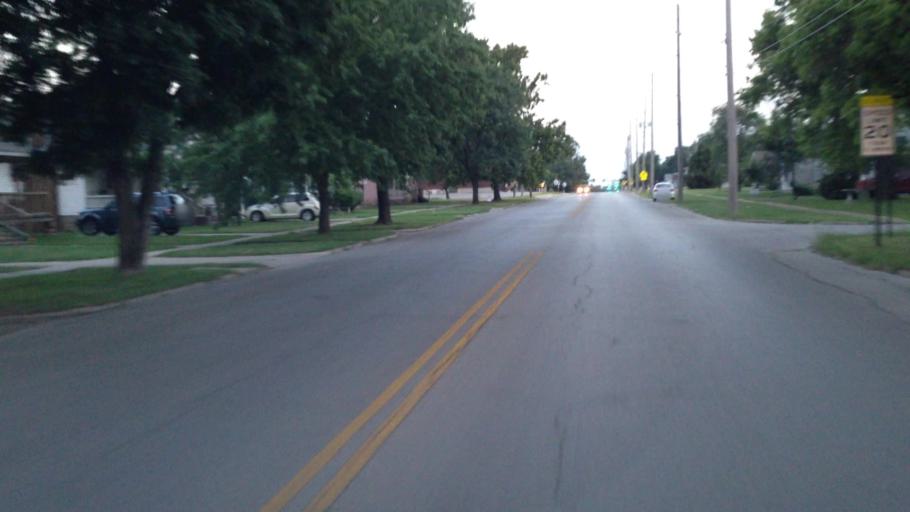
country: US
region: Kansas
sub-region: Montgomery County
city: Independence
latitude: 37.2301
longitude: -95.7108
